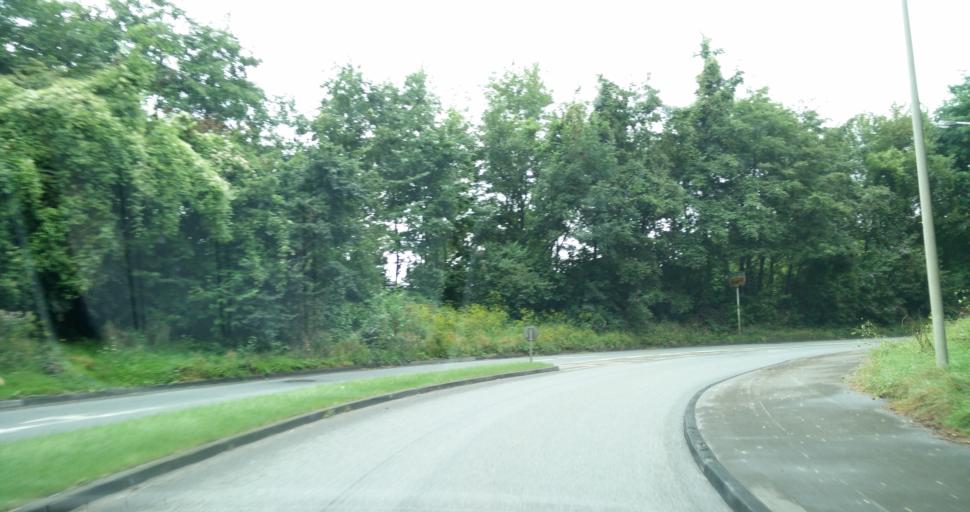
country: DE
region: North Rhine-Westphalia
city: Wulfrath
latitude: 51.2515
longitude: 7.0601
